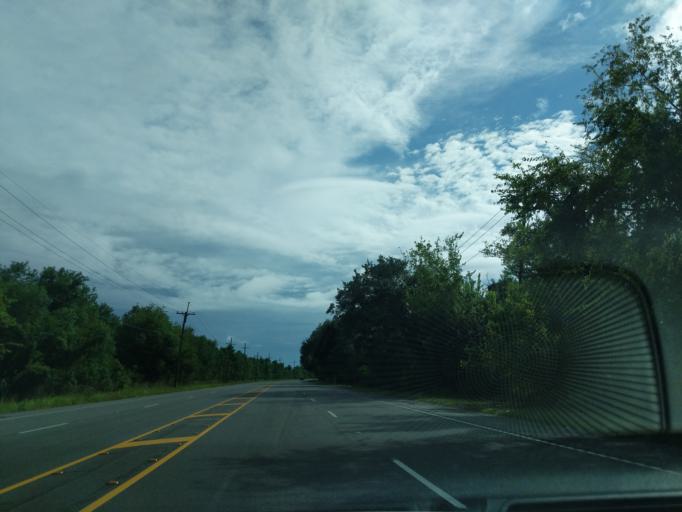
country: US
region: Louisiana
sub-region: Saint Bernard Parish
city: Meraux
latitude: 30.0685
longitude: -89.8642
